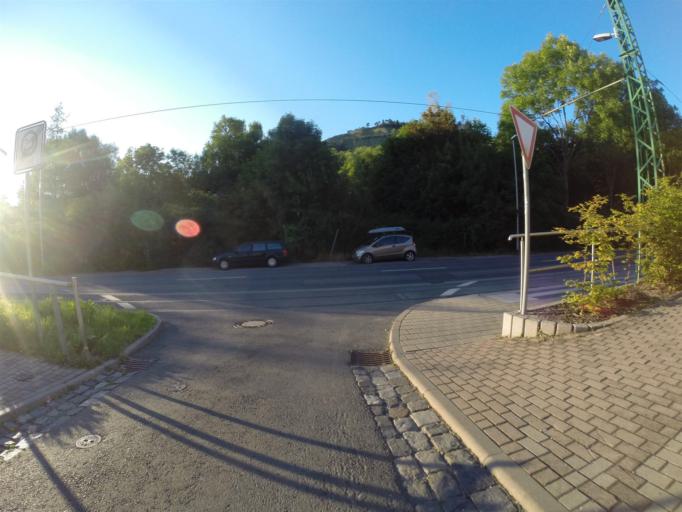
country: DE
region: Thuringia
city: Jena
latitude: 50.9335
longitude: 11.6196
